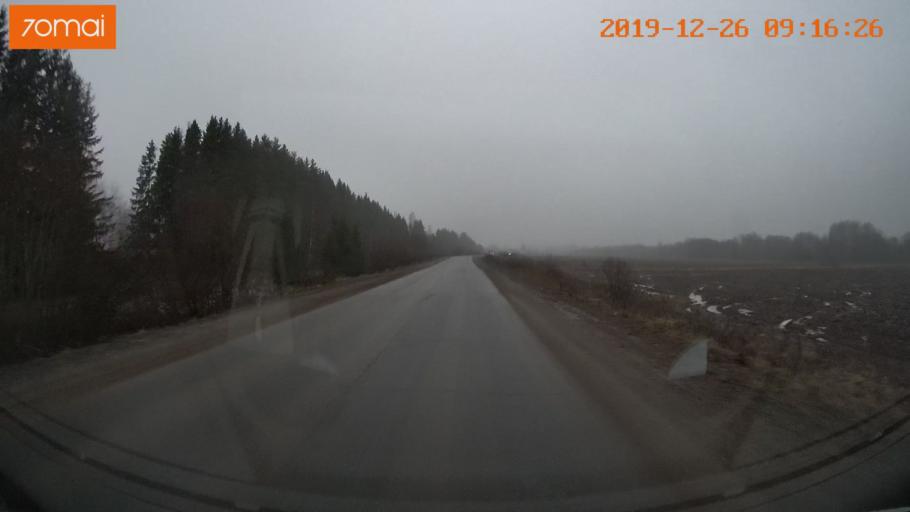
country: RU
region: Vologda
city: Gryazovets
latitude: 58.9183
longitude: 40.2389
